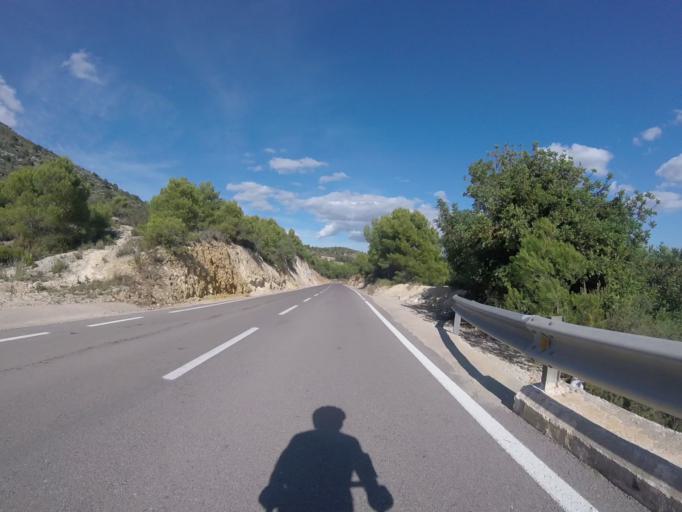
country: ES
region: Valencia
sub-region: Provincia de Castello
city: Alcala de Xivert
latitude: 40.3009
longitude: 0.1889
